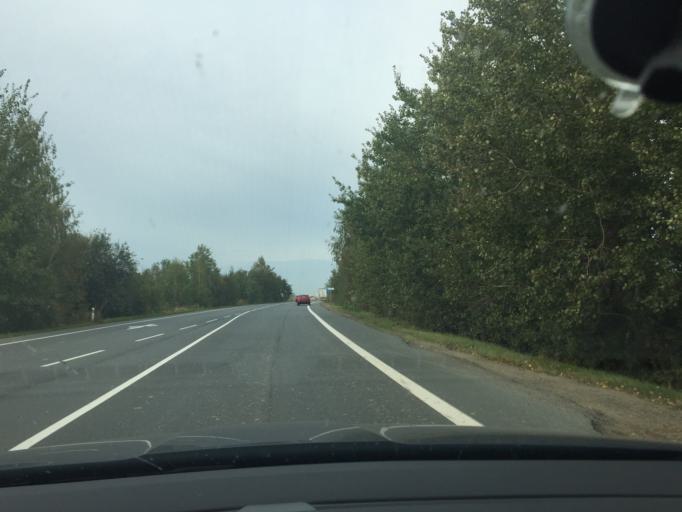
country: CZ
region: Central Bohemia
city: Jirny
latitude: 50.1240
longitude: 14.7037
